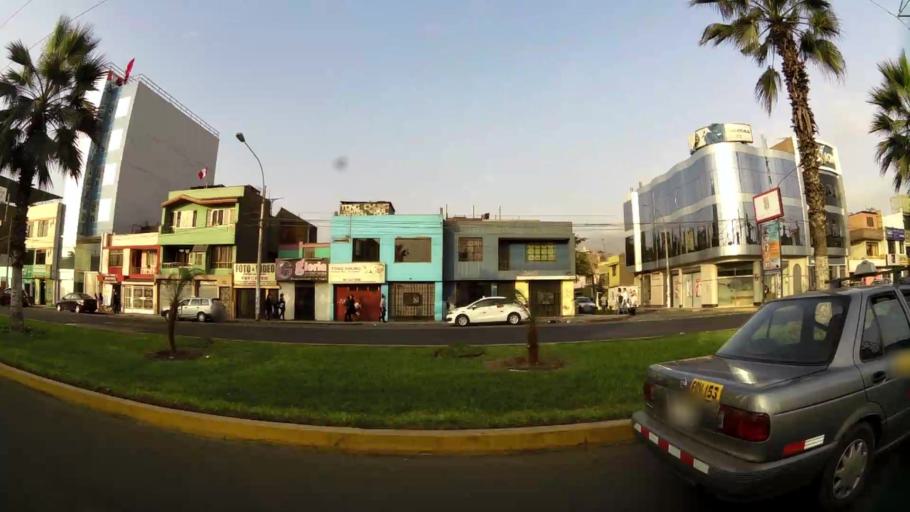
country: PE
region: Lima
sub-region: Lima
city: Independencia
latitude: -11.9886
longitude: -77.0718
